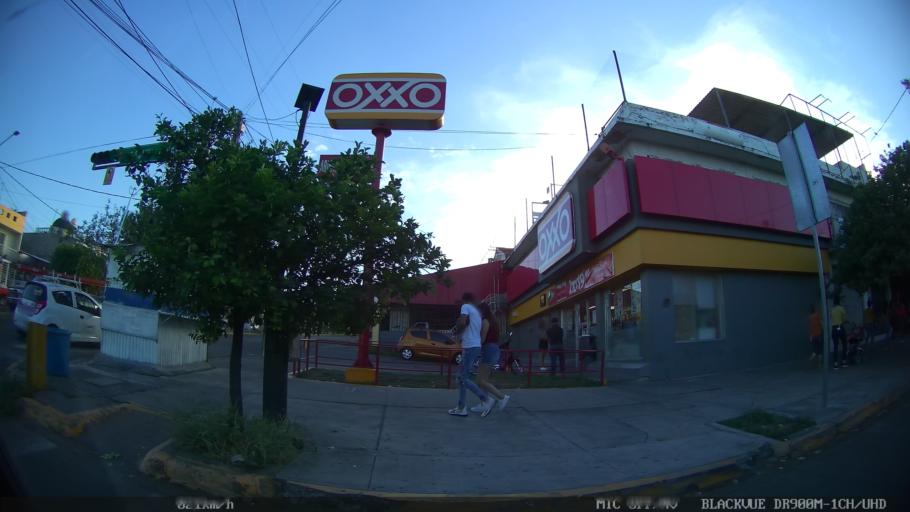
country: MX
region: Jalisco
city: Tlaquepaque
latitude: 20.7004
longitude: -103.2911
